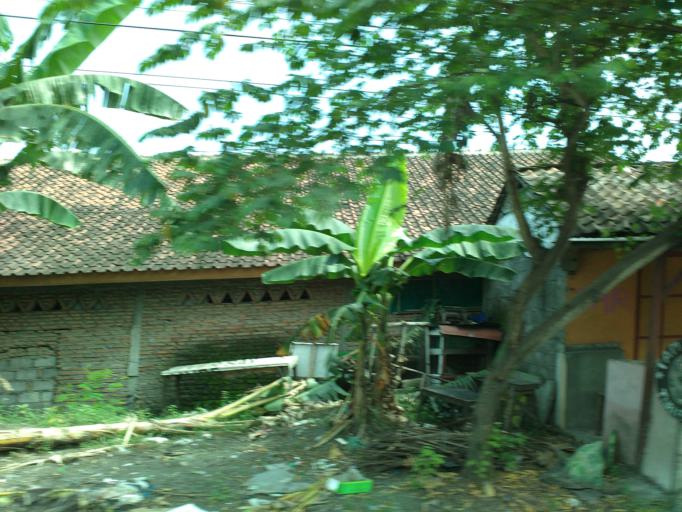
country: ID
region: Central Java
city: Candi Prambanan
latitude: -7.7544
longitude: 110.5135
